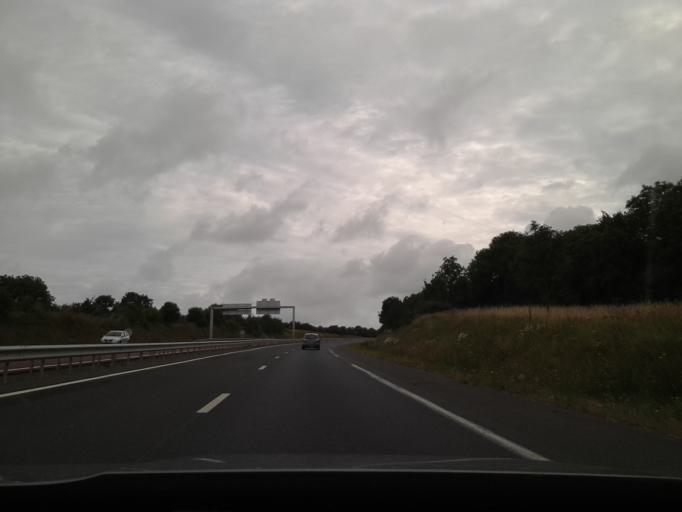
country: FR
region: Lower Normandy
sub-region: Departement du Calvados
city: Isigny-sur-Mer
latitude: 49.3366
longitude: -1.0616
